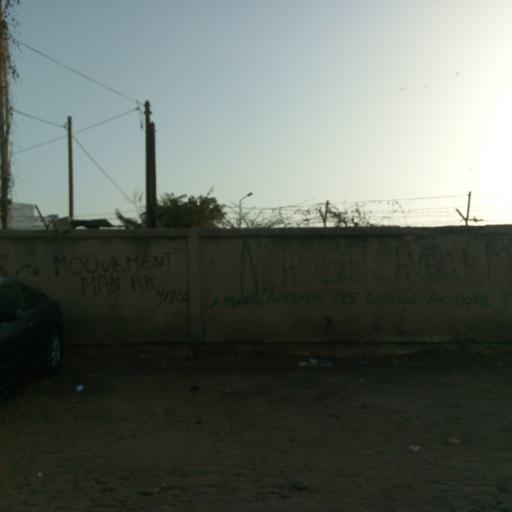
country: SN
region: Dakar
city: Dakar
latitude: 14.6964
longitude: -17.4508
